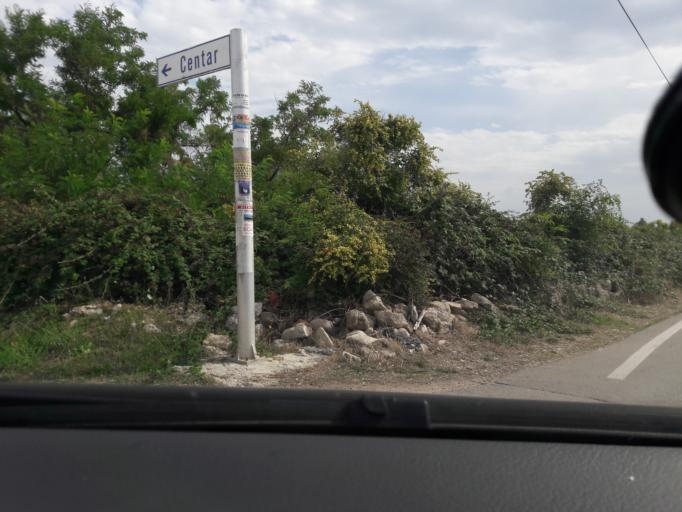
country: HR
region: Zadarska
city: Vir
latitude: 44.2975
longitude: 15.0765
